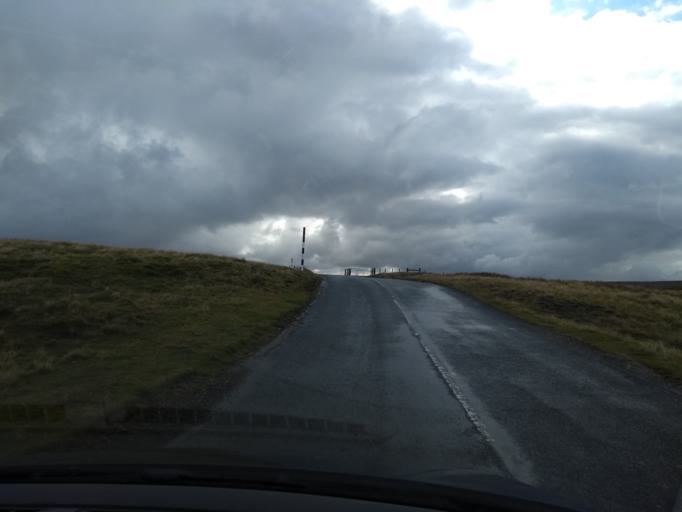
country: GB
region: England
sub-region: Cumbria
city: Kirkby Stephen
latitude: 54.3558
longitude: -2.2043
